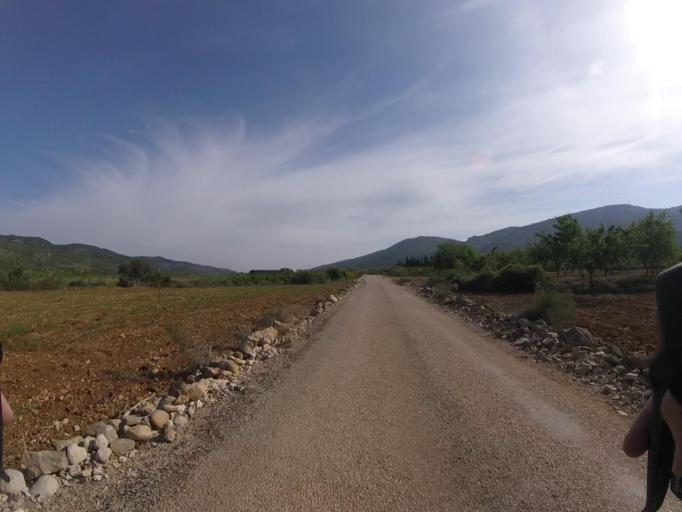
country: ES
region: Valencia
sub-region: Provincia de Castello
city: Alcala de Xivert
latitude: 40.2813
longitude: 0.2606
